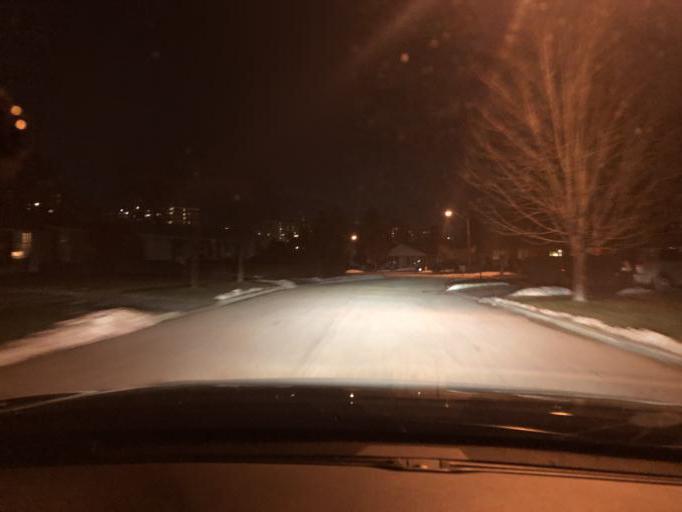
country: CA
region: Ontario
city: Scarborough
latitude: 43.7780
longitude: -79.3012
